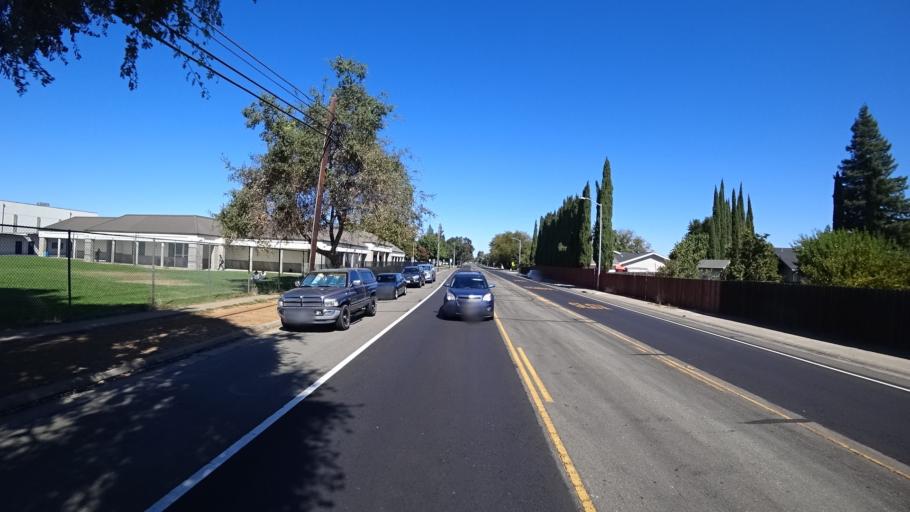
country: US
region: California
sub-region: Sacramento County
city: Elk Grove
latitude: 38.3990
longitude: -121.3715
